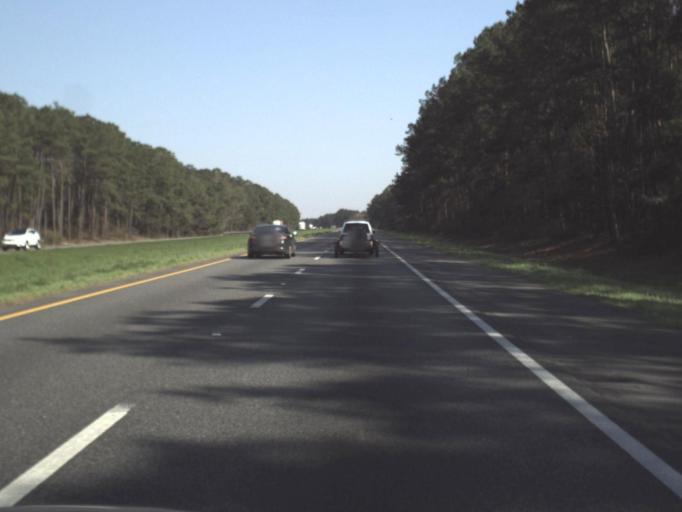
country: US
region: Florida
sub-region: Gadsden County
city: Quincy
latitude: 30.5332
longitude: -84.5781
